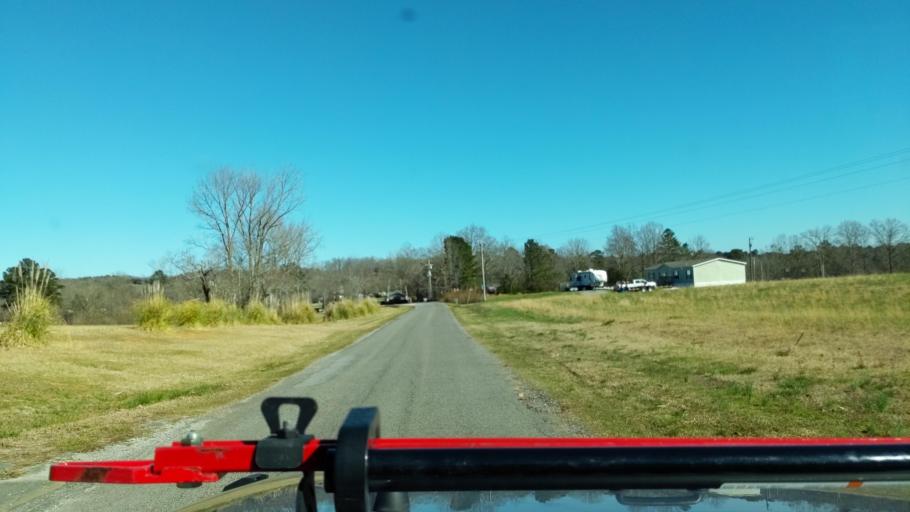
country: US
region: Alabama
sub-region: Walker County
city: Jasper
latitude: 34.0546
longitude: -87.1486
